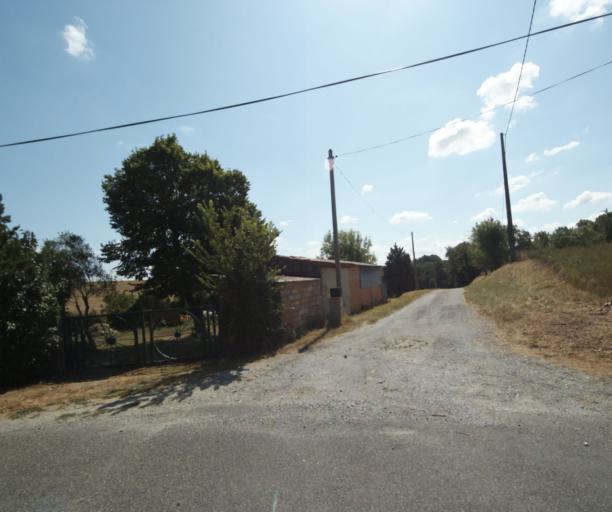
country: FR
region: Midi-Pyrenees
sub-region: Departement de la Haute-Garonne
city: Auriac-sur-Vendinelle
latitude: 43.4598
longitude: 1.7880
